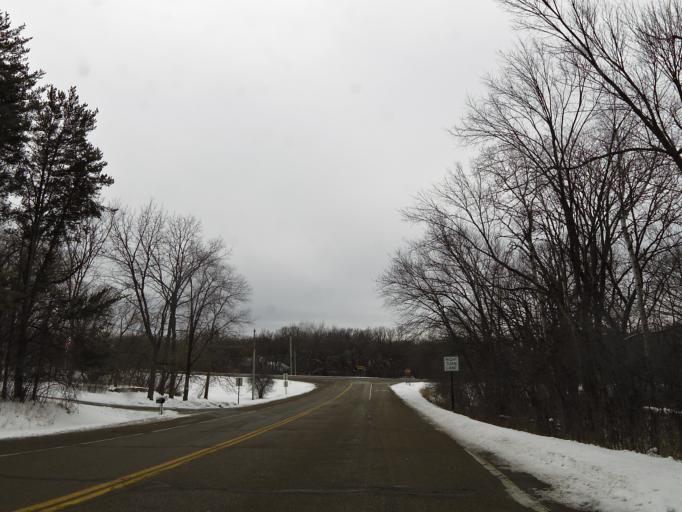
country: US
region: Minnesota
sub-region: Washington County
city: Lakeland
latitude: 44.9644
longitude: -92.8224
